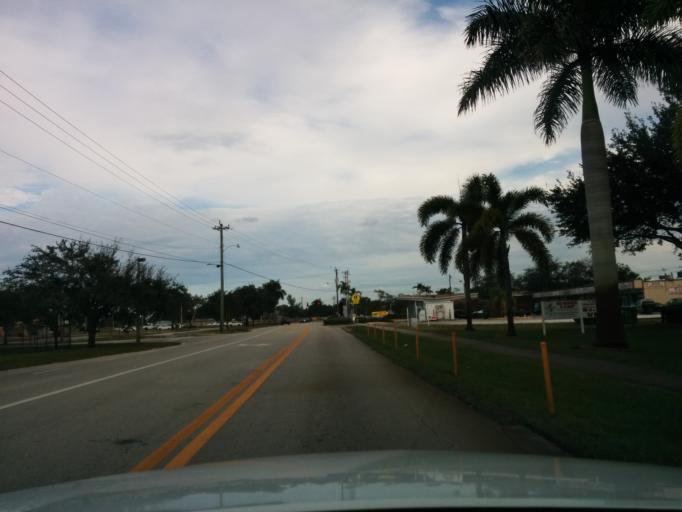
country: US
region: Florida
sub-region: Broward County
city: Davie
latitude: 26.0730
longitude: -80.2343
